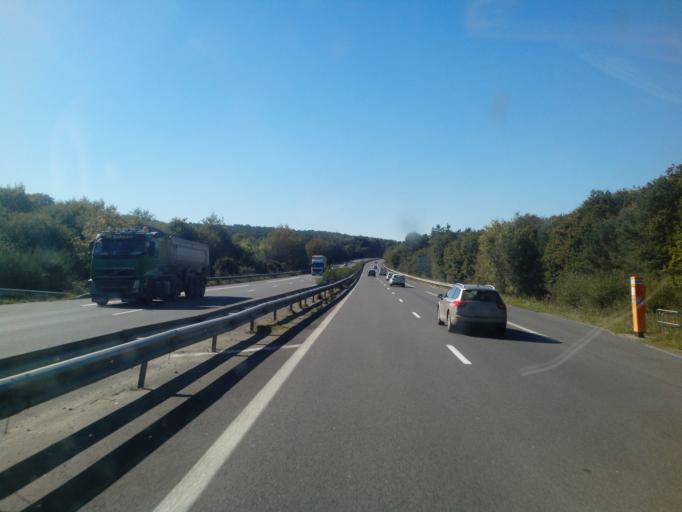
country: FR
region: Pays de la Loire
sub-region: Departement de la Loire-Atlantique
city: La Chapelle-des-Marais
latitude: 47.4860
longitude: -2.2110
